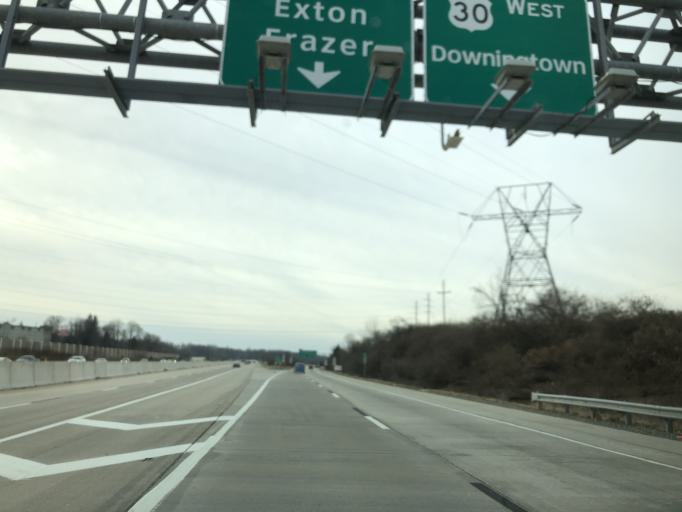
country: US
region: Pennsylvania
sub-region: Chester County
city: Exton
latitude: 40.0384
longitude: -75.5814
